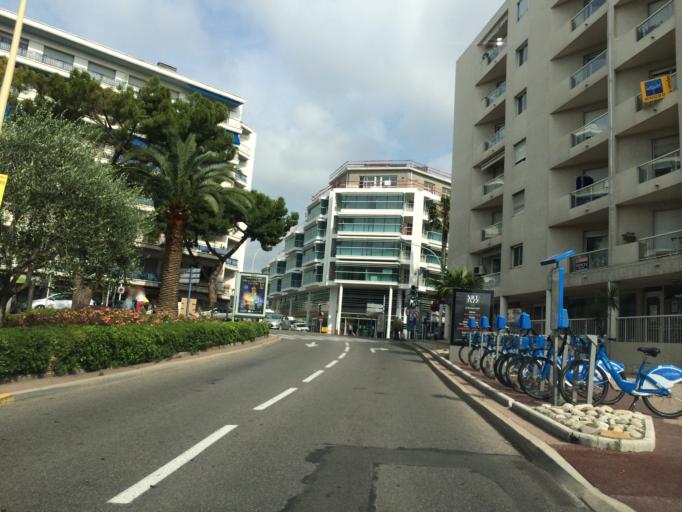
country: FR
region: Provence-Alpes-Cote d'Azur
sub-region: Departement des Alpes-Maritimes
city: Cagnes-sur-Mer
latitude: 43.6574
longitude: 7.1516
